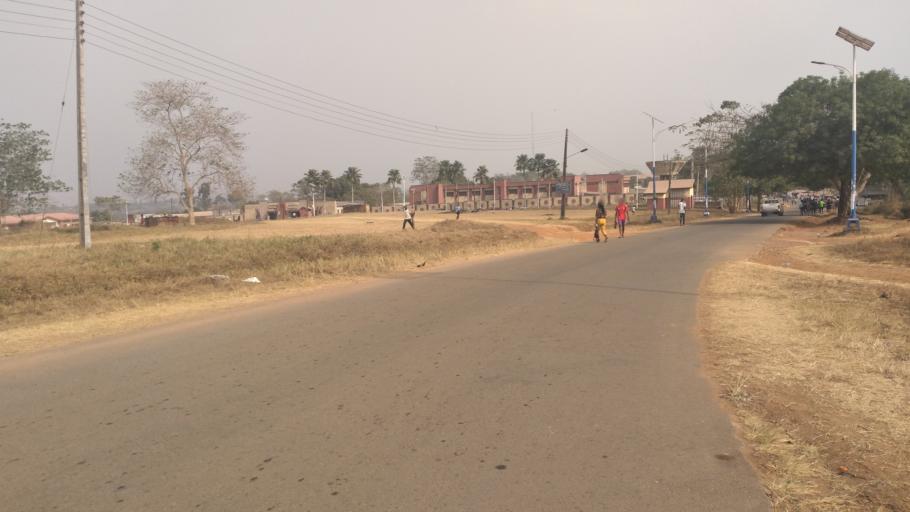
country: NG
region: Ondo
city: Ilare
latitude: 7.3047
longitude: 5.1400
